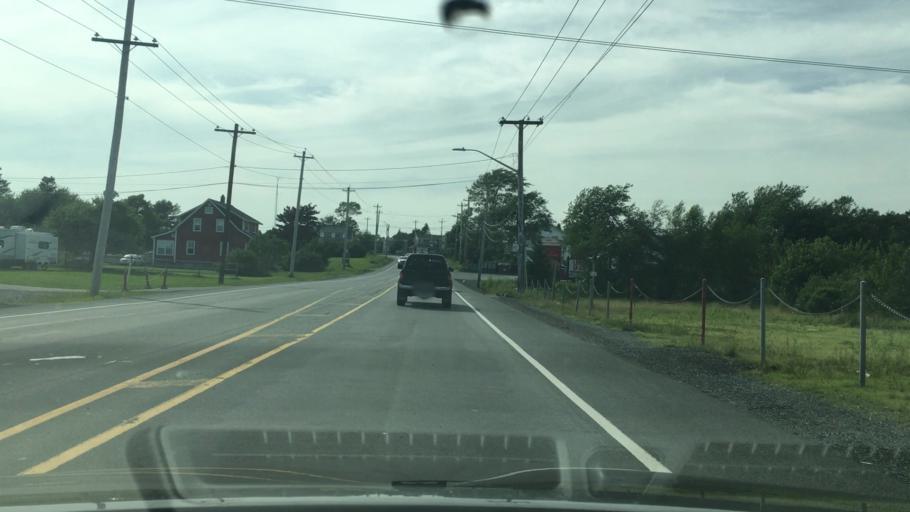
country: CA
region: Nova Scotia
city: Dartmouth
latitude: 44.7327
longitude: -63.7605
